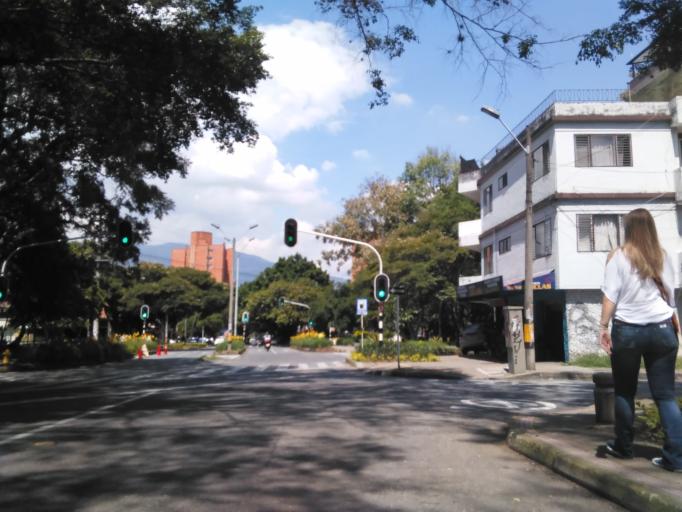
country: CO
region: Antioquia
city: Medellin
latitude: 6.2349
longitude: -75.5963
